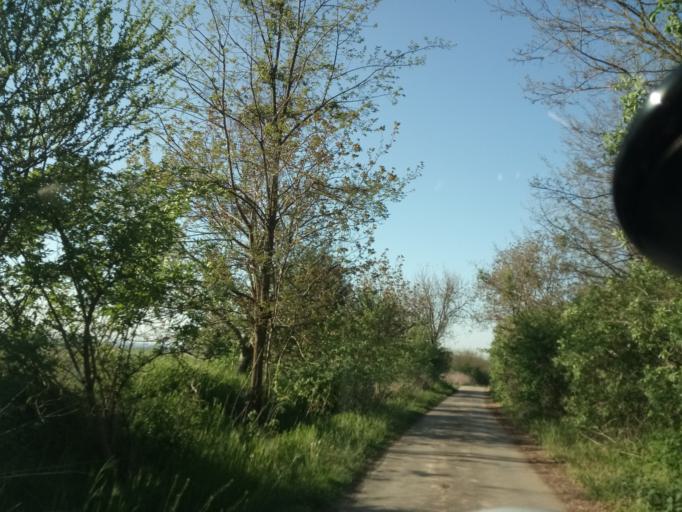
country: HU
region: Zala
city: Sarmellek
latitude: 46.7178
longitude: 17.0957
